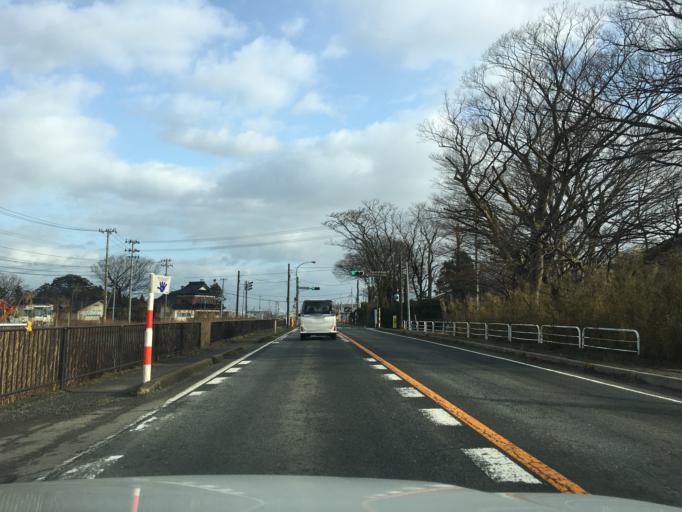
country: JP
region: Yamagata
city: Sakata
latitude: 38.8439
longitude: 139.8488
